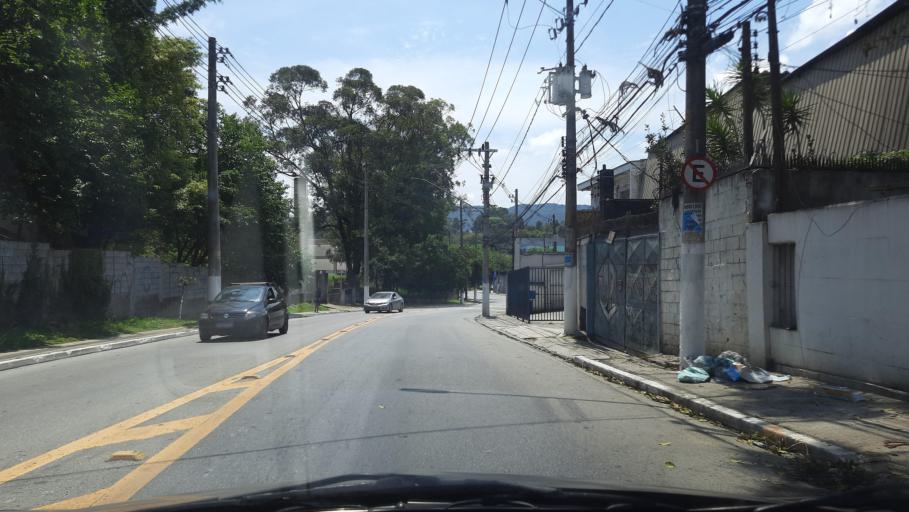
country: BR
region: Sao Paulo
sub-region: Caieiras
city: Caieiras
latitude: -23.4477
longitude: -46.7324
